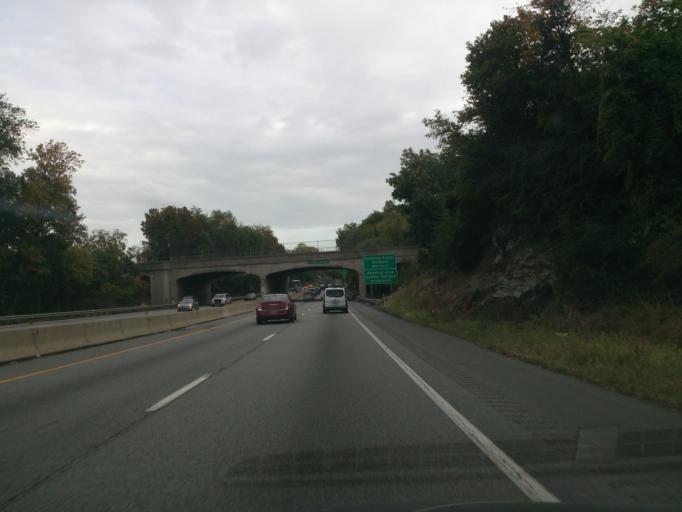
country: US
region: Pennsylvania
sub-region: Berks County
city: West Reading
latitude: 40.3392
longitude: -75.9450
